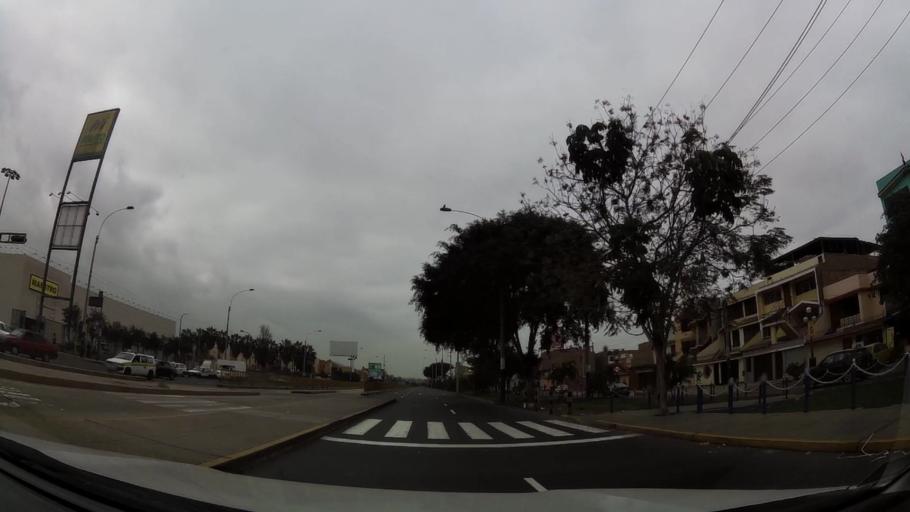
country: PE
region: Lima
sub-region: Lima
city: Surco
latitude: -12.1740
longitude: -77.0144
